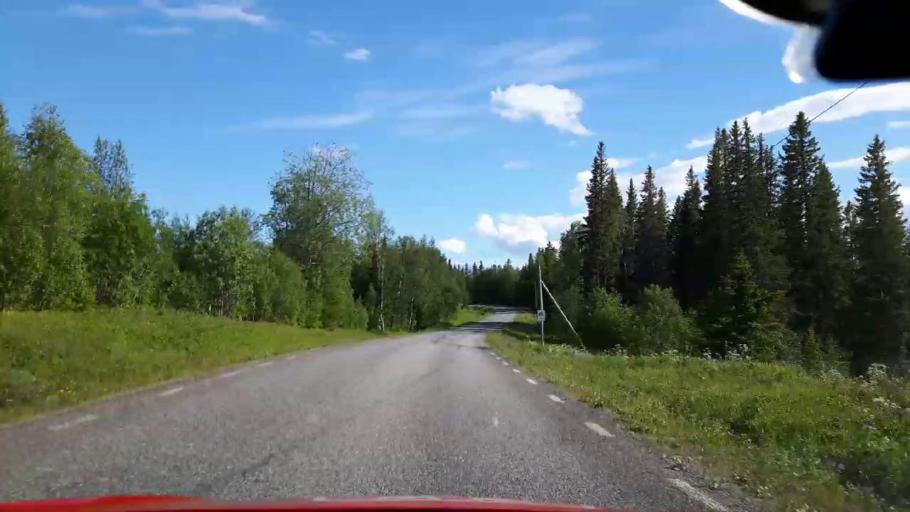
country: SE
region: Jaemtland
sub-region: Krokoms Kommun
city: Valla
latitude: 63.7046
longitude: 14.1457
